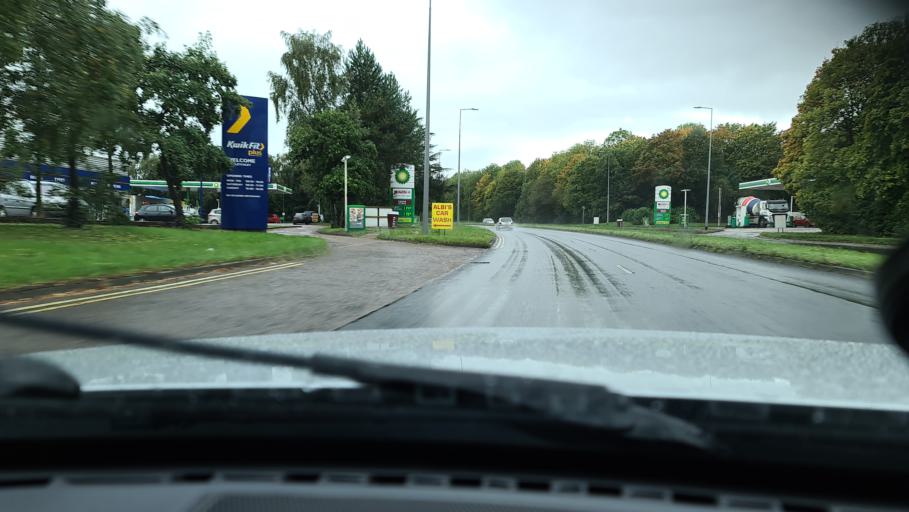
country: GB
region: England
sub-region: Buckinghamshire
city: Bletchley
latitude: 51.9994
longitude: -0.7316
